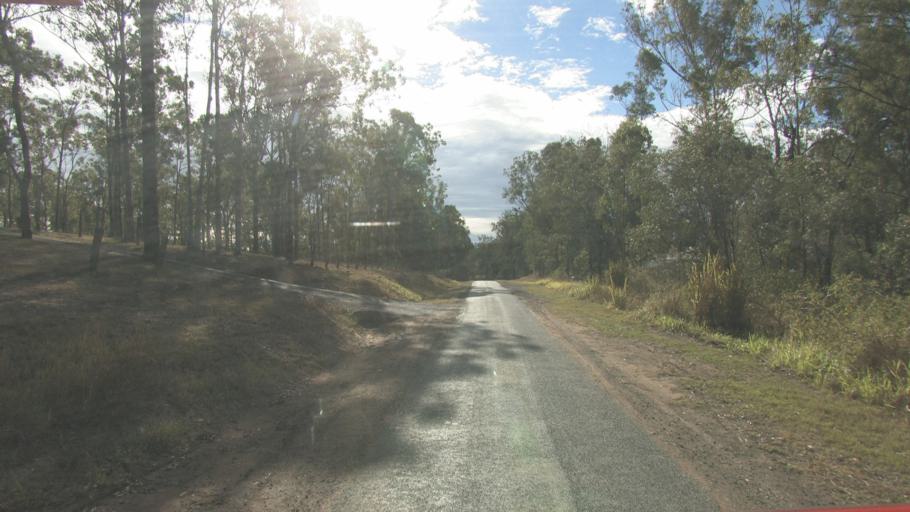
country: AU
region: Queensland
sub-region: Logan
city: Cedar Vale
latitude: -27.8421
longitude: 153.0686
